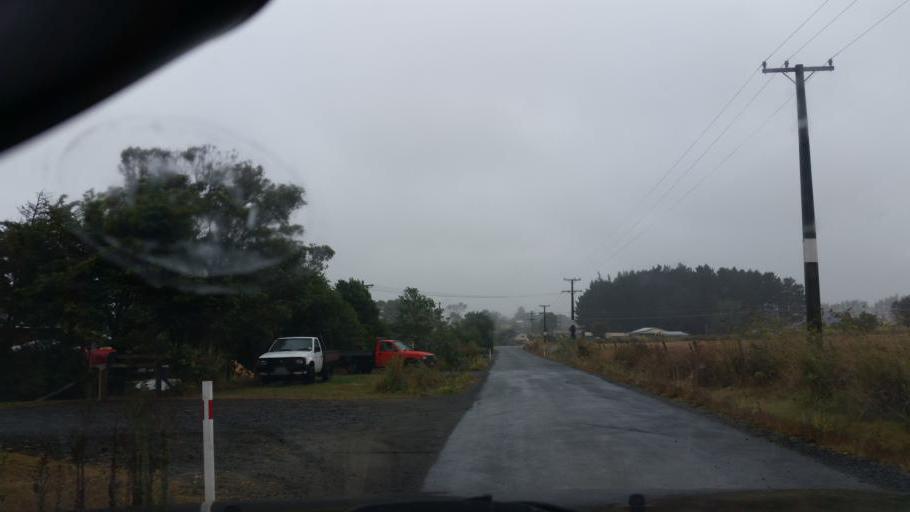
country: NZ
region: Northland
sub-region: Kaipara District
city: Dargaville
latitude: -35.9194
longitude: 173.8172
